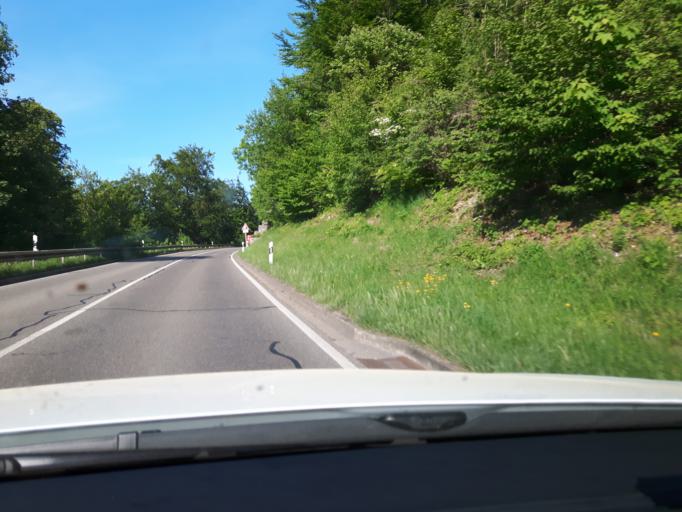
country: DE
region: Baden-Wuerttemberg
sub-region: Tuebingen Region
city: Pfullingen
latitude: 48.4386
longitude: 9.2624
